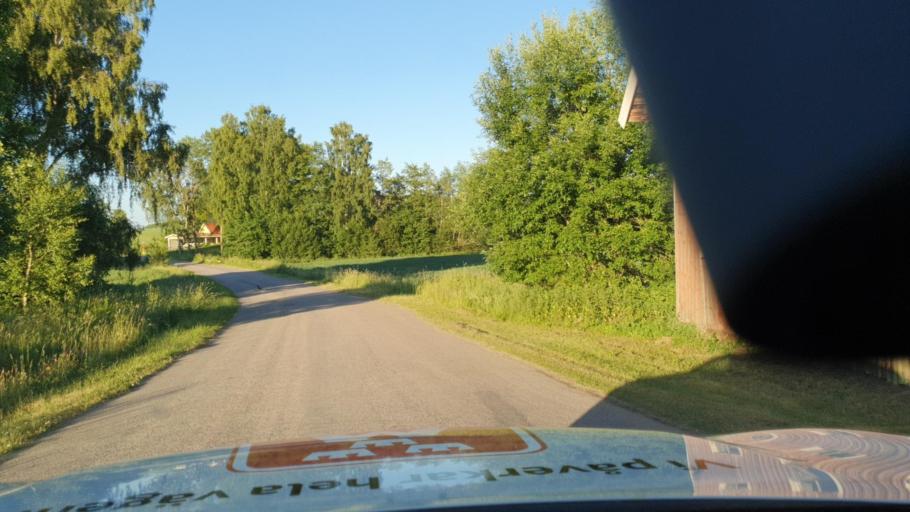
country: SE
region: Vaestra Goetaland
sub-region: Skovde Kommun
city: Skoevde
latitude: 58.3709
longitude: 13.8807
